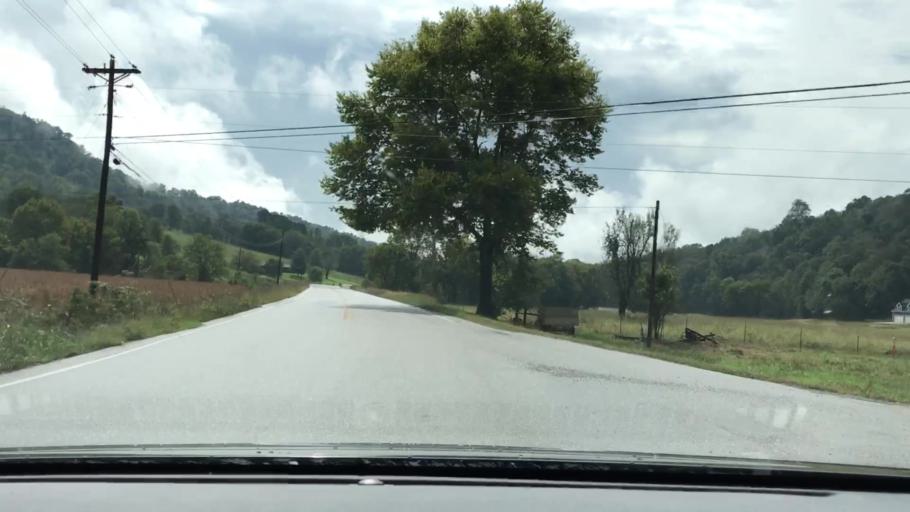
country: US
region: Tennessee
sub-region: Smith County
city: Carthage
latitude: 36.3630
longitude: -85.9551
